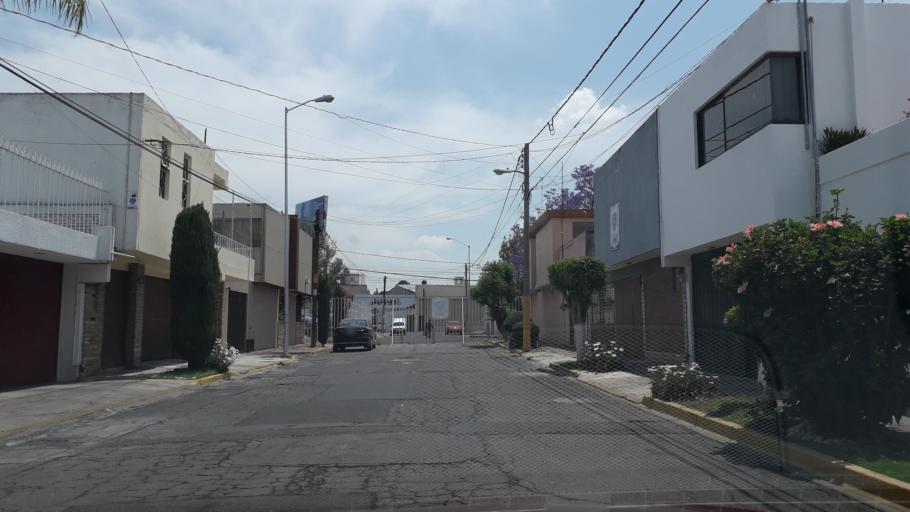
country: MX
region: Puebla
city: Puebla
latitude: 19.0232
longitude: -98.1927
